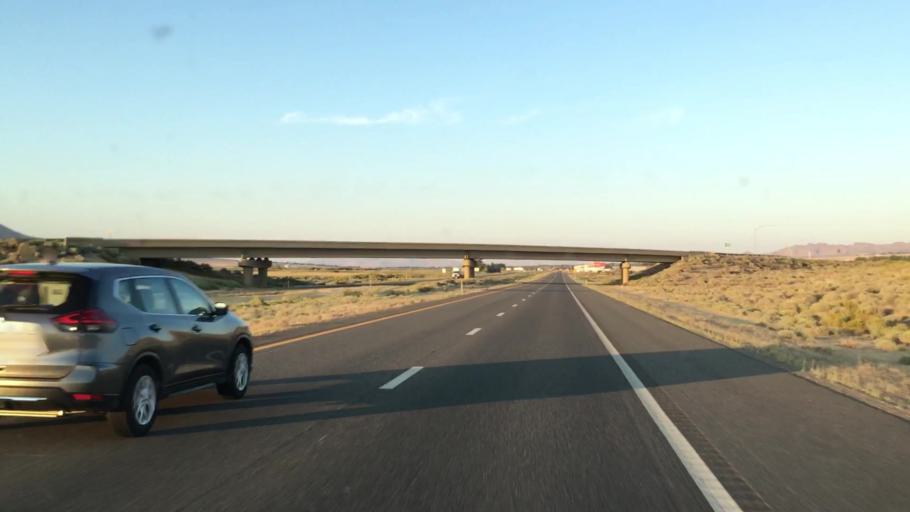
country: US
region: Nevada
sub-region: Humboldt County
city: Winnemucca
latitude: 40.9296
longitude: -117.8059
